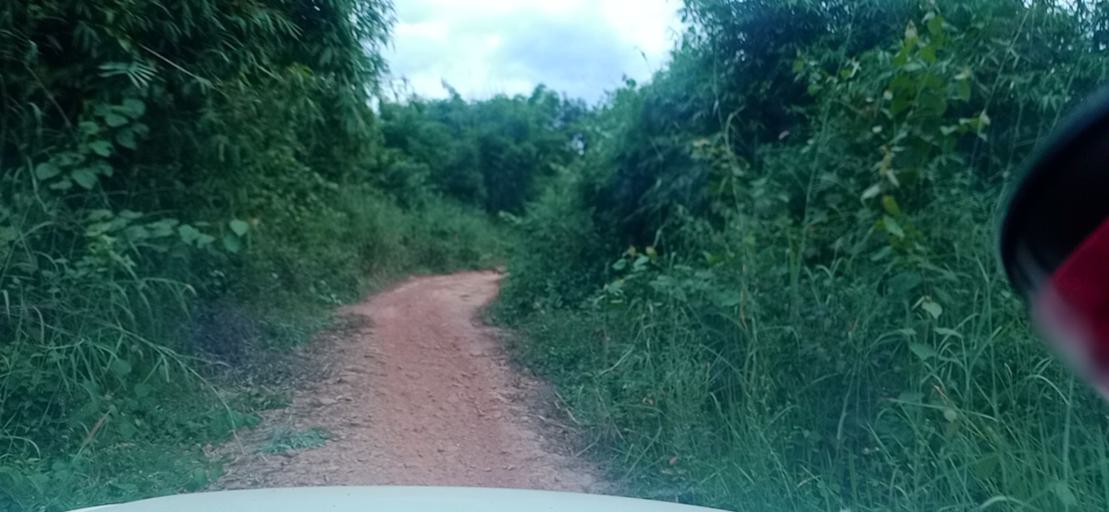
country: TH
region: Changwat Bueng Kan
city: Pak Khat
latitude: 18.5637
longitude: 103.2805
